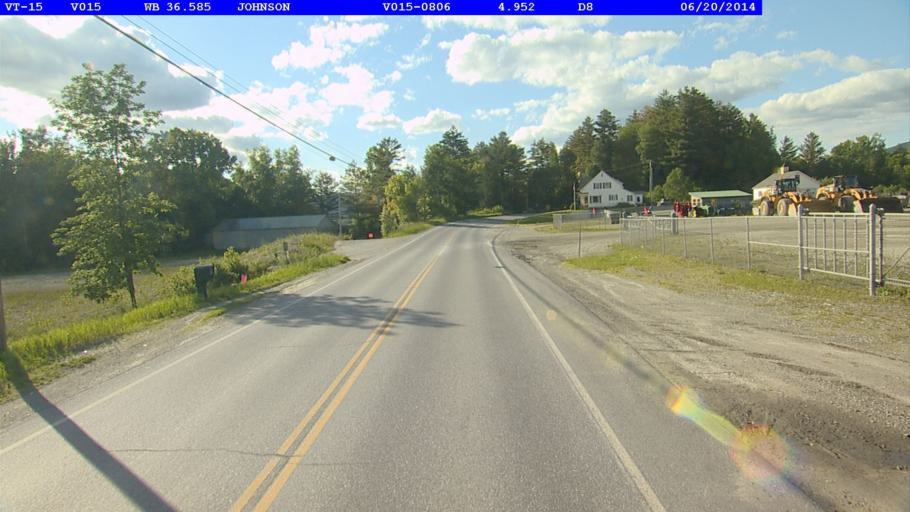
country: US
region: Vermont
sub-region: Lamoille County
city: Johnson
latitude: 44.6250
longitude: -72.6770
